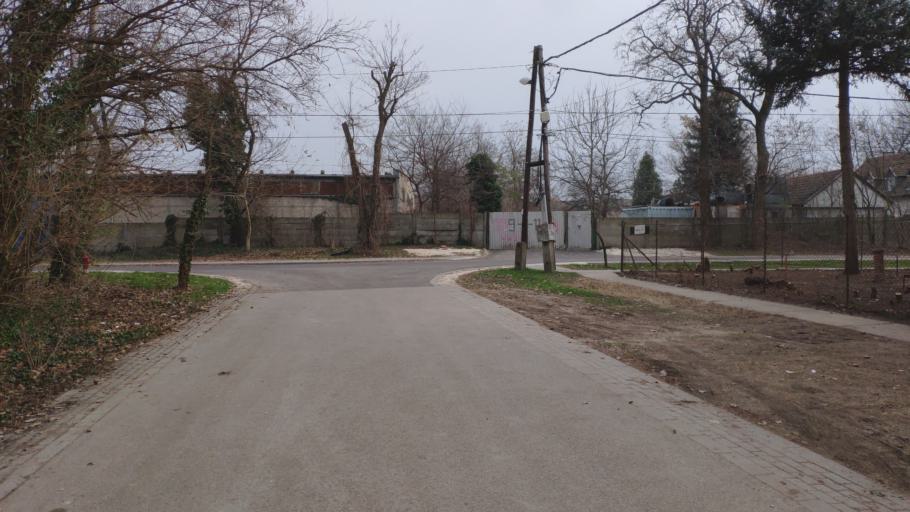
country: HU
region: Budapest
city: Budapest XVI. keruelet
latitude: 47.5110
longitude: 19.1583
